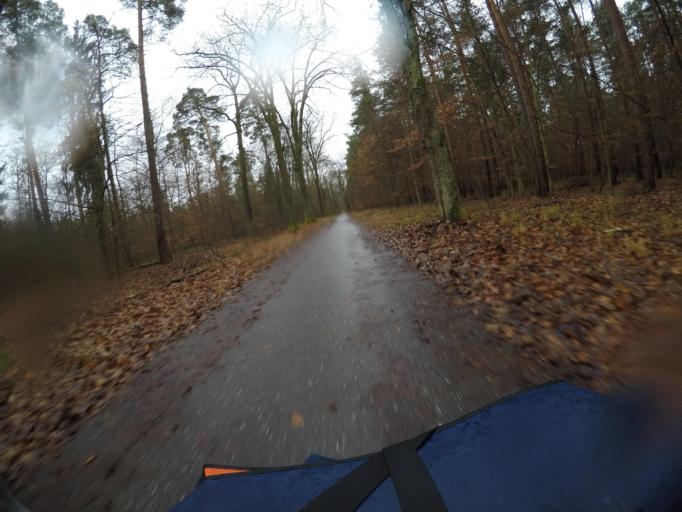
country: DE
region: Baden-Wuerttemberg
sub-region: Karlsruhe Region
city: Eggenstein-Leopoldshafen
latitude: 49.0889
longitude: 8.4609
